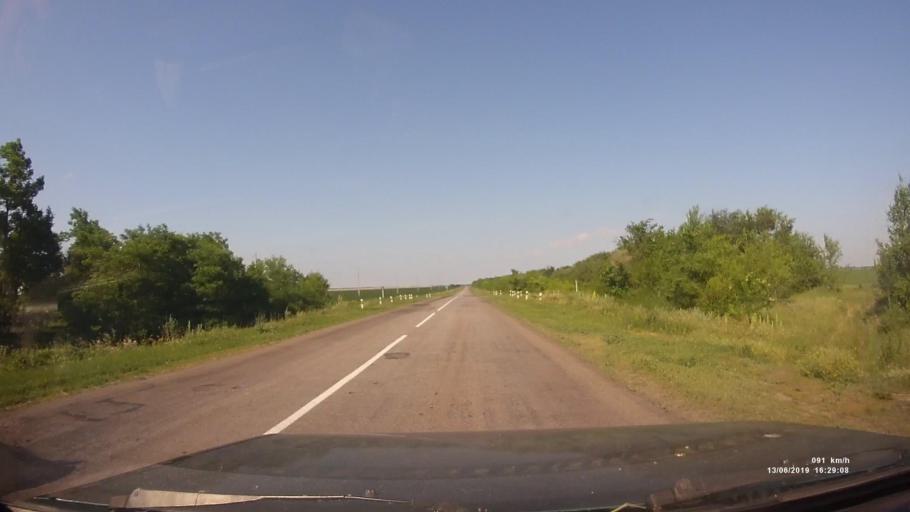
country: RU
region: Rostov
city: Kazanskaya
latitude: 49.8274
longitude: 41.2120
